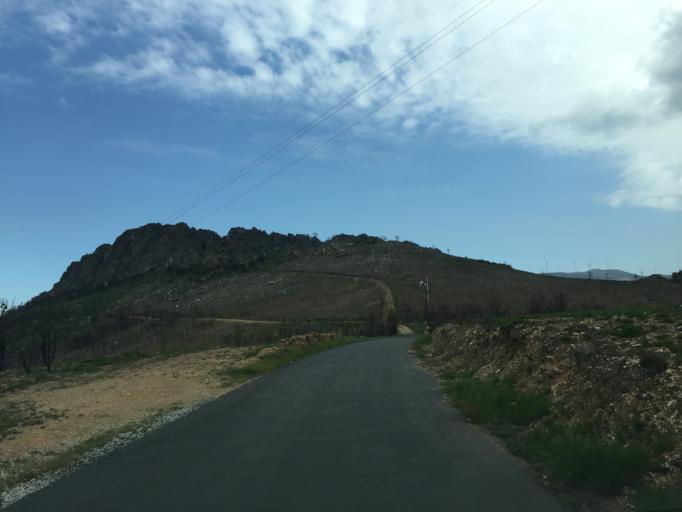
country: PT
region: Coimbra
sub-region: Pampilhosa da Serra
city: Pampilhosa da Serra
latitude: 40.1499
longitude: -7.9269
